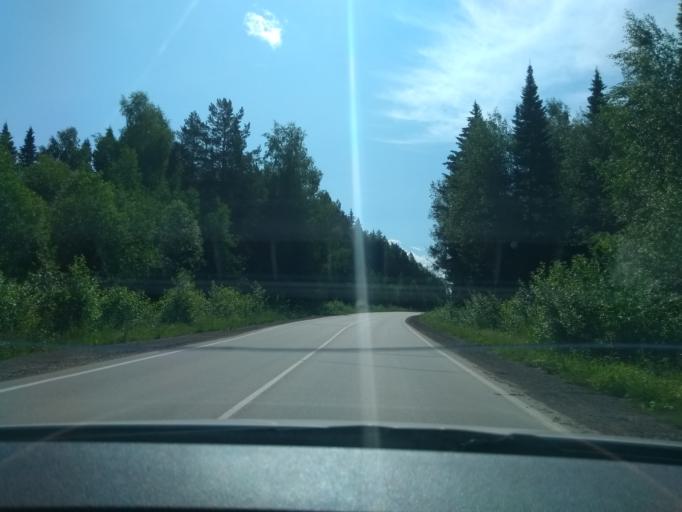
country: RU
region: Perm
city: Lobanovo
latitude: 57.8329
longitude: 56.4031
